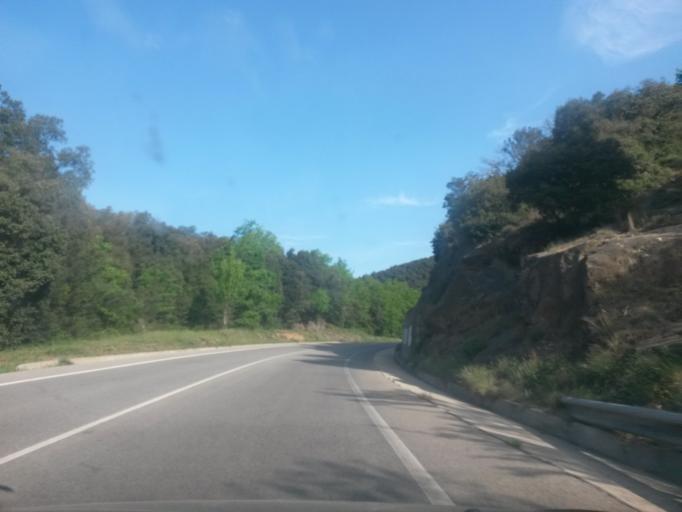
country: ES
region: Catalonia
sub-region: Provincia de Girona
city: Sant Feliu de Pallerols
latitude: 42.0691
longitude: 2.5241
